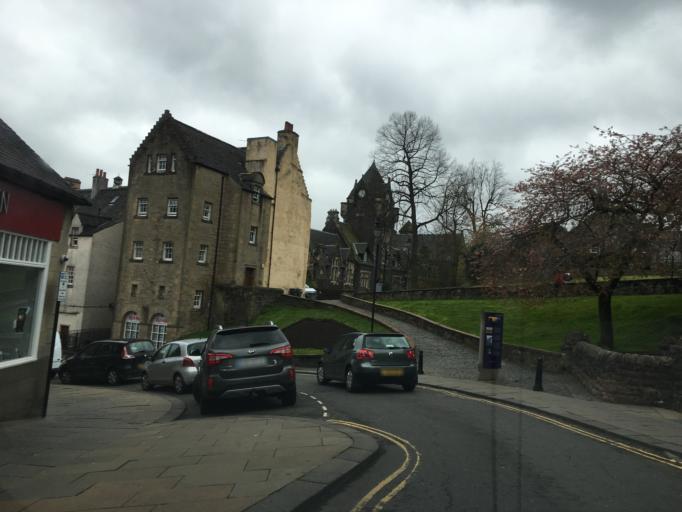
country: GB
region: Scotland
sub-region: Stirling
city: Stirling
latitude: 56.1203
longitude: -3.9418
